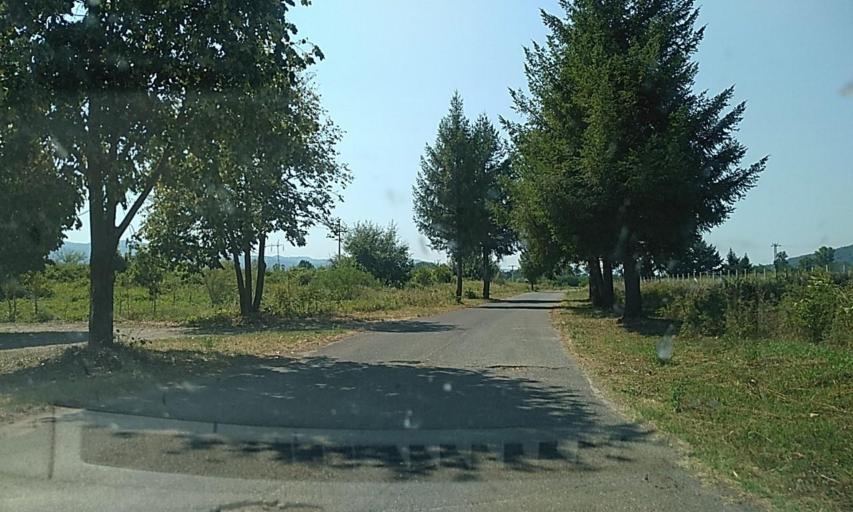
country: RS
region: Central Serbia
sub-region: Pcinjski Okrug
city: Vladicin Han
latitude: 42.6640
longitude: 22.0504
